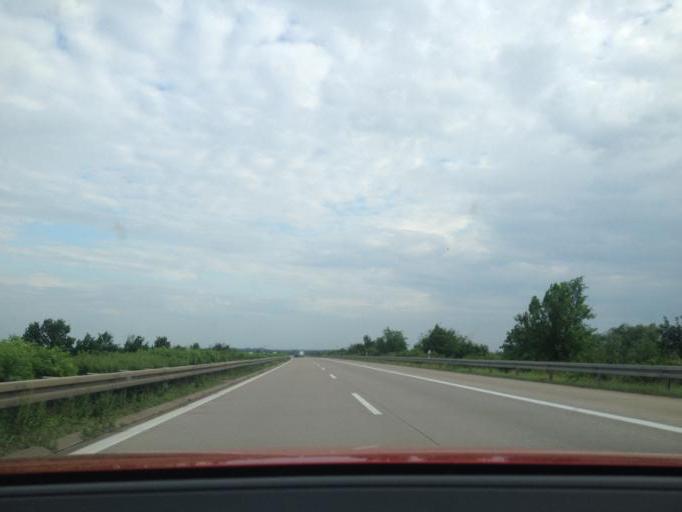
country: DE
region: Saxony-Anhalt
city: Oppin
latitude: 51.5339
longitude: 12.0159
